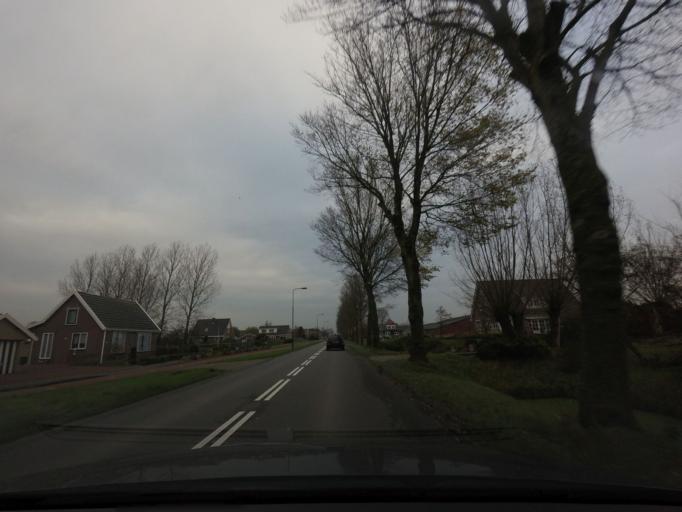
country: NL
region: North Holland
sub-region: Gemeente Heerhugowaard
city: Heerhugowaard
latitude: 52.6916
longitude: 4.8505
